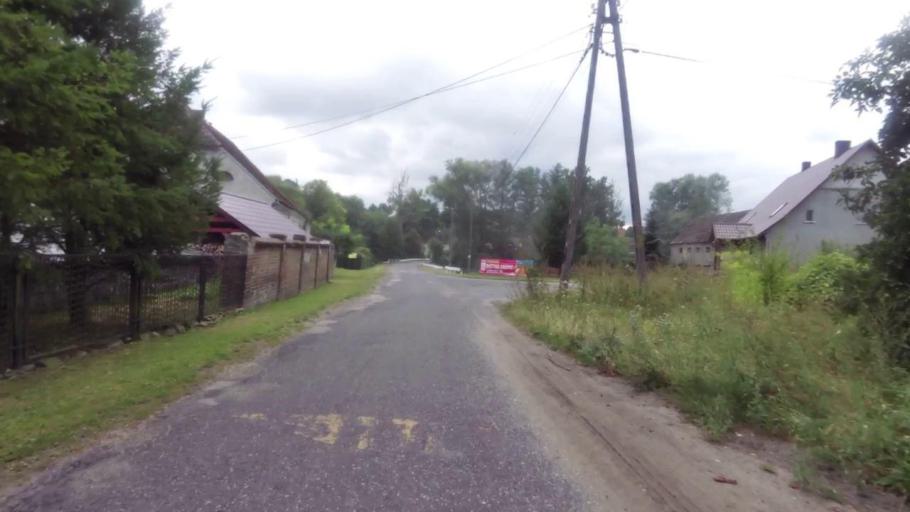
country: PL
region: West Pomeranian Voivodeship
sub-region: Powiat mysliborski
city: Boleszkowice
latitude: 52.6799
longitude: 14.6215
